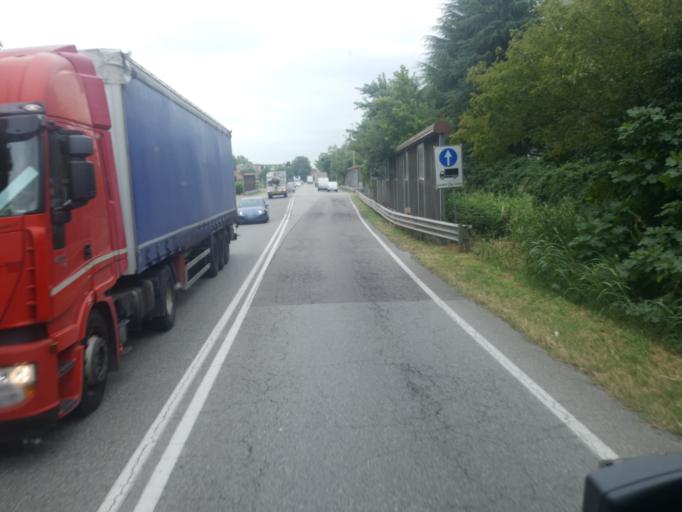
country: IT
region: Lombardy
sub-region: Citta metropolitana di Milano
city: Melzo
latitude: 45.4941
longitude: 9.4209
